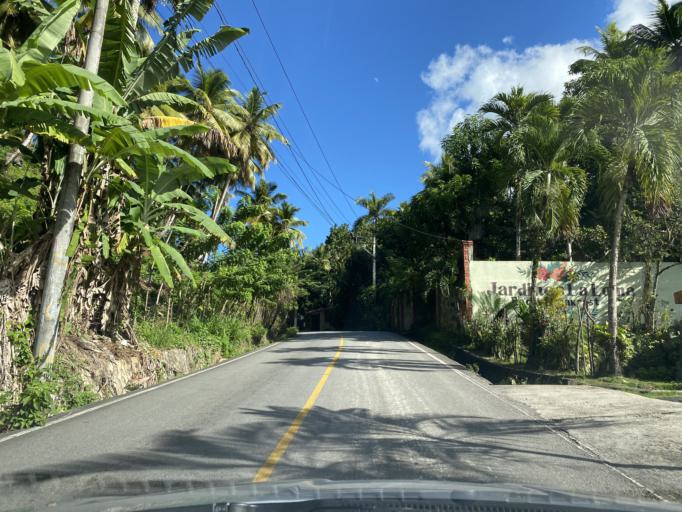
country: DO
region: Samana
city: Sanchez
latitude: 19.2336
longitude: -69.6022
